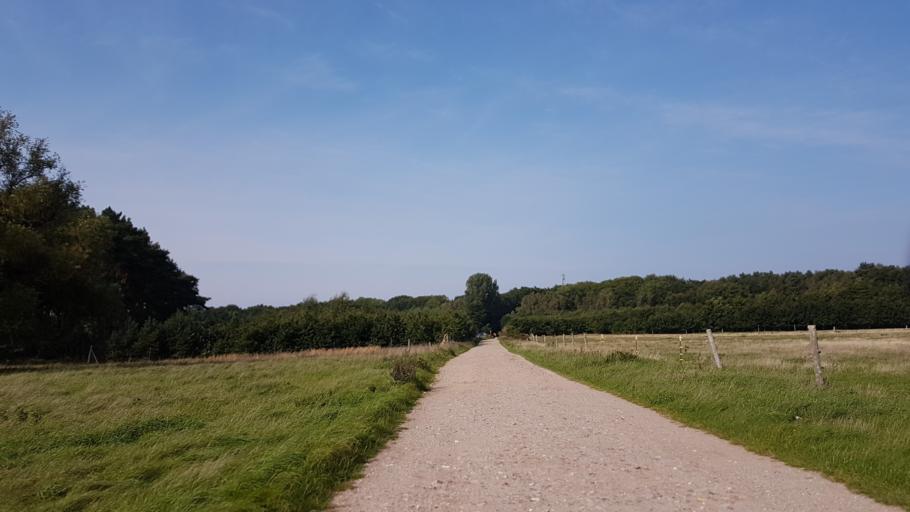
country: DE
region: Mecklenburg-Vorpommern
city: Glowe
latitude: 54.5582
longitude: 13.4628
